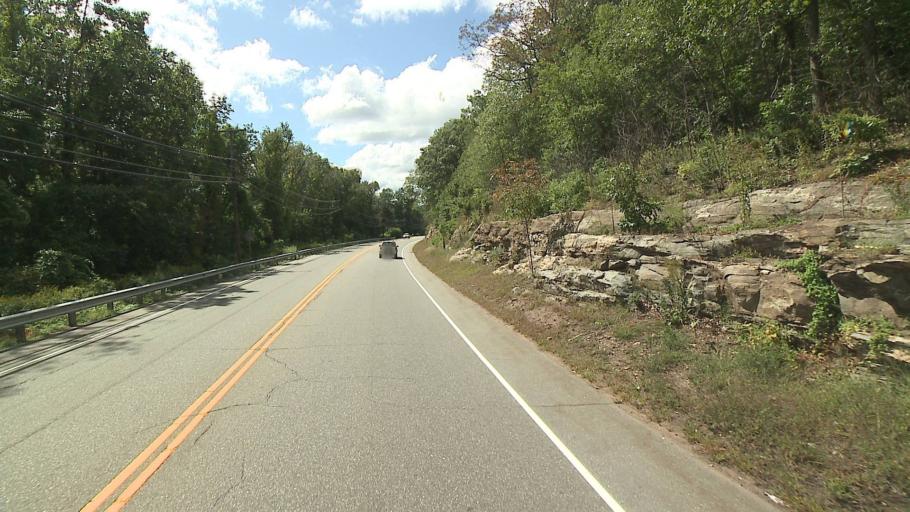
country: US
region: Connecticut
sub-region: Tolland County
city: Rockville
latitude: 41.7936
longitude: -72.4381
